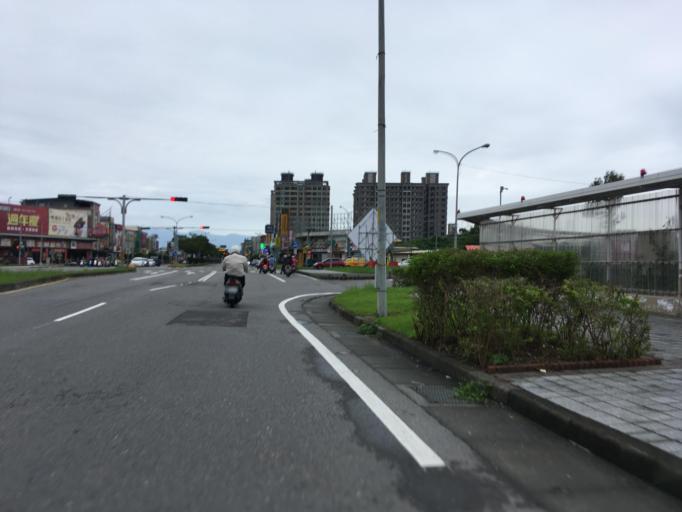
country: TW
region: Taiwan
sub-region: Yilan
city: Yilan
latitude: 24.6869
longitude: 121.7709
